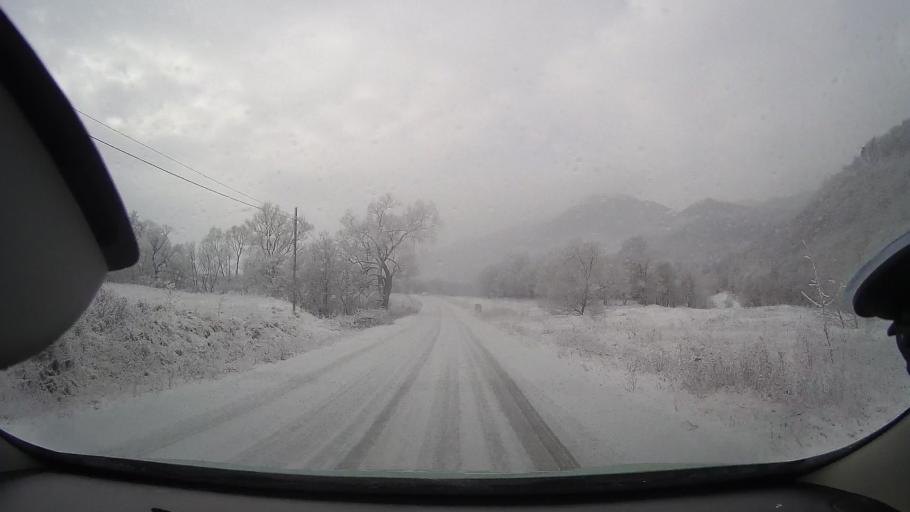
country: RO
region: Alba
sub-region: Comuna Rimetea
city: Rimetea
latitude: 46.4687
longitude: 23.5797
